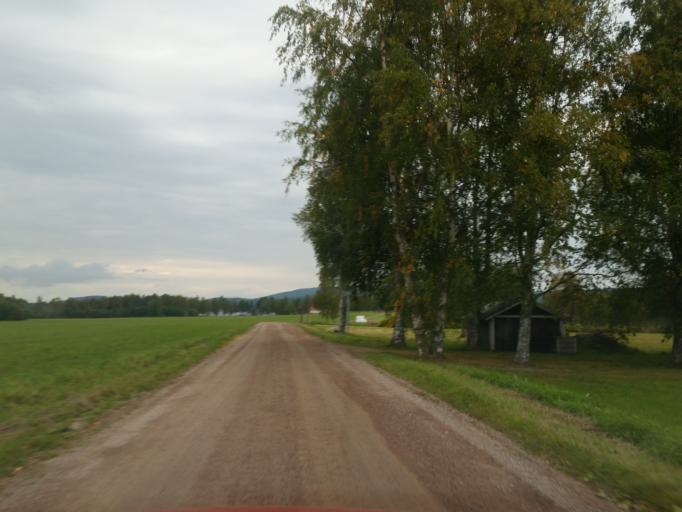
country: SE
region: Dalarna
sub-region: Leksand Municipality
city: Smedby
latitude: 60.6754
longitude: 15.1412
